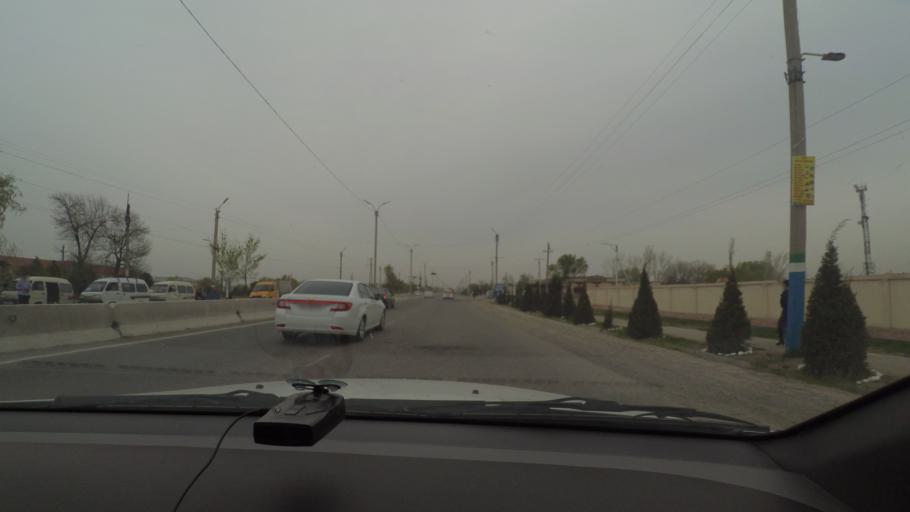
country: KZ
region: Ongtustik Qazaqstan
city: Myrzakent
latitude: 40.5431
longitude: 68.4158
